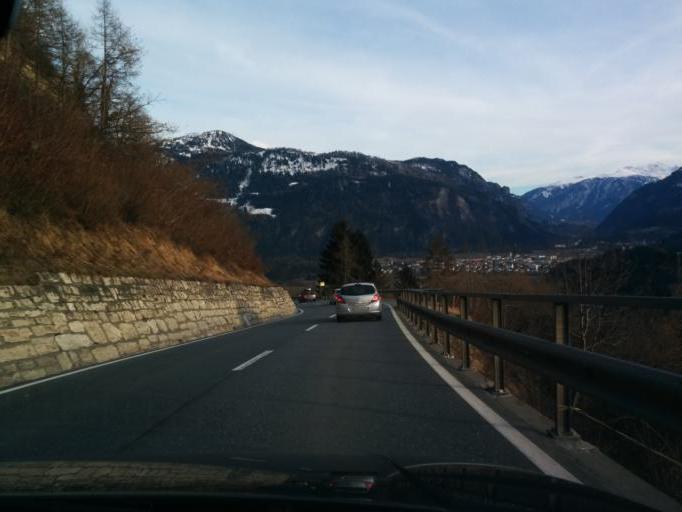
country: CH
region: Grisons
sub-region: Imboden District
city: Bonaduz
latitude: 46.8279
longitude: 9.3808
